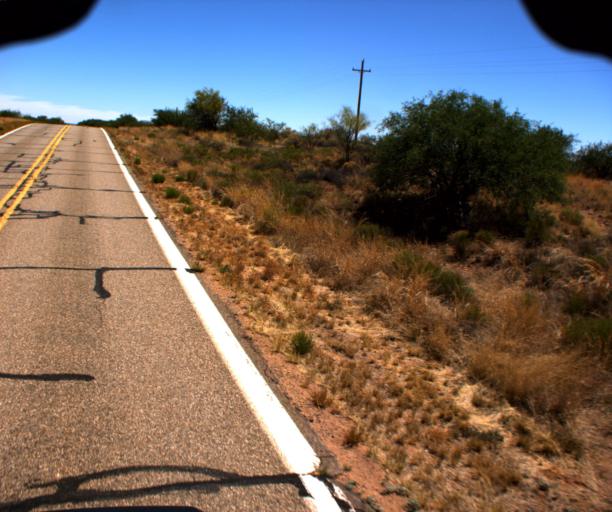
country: US
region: Arizona
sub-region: Pima County
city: Three Points
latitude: 31.7108
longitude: -111.4878
